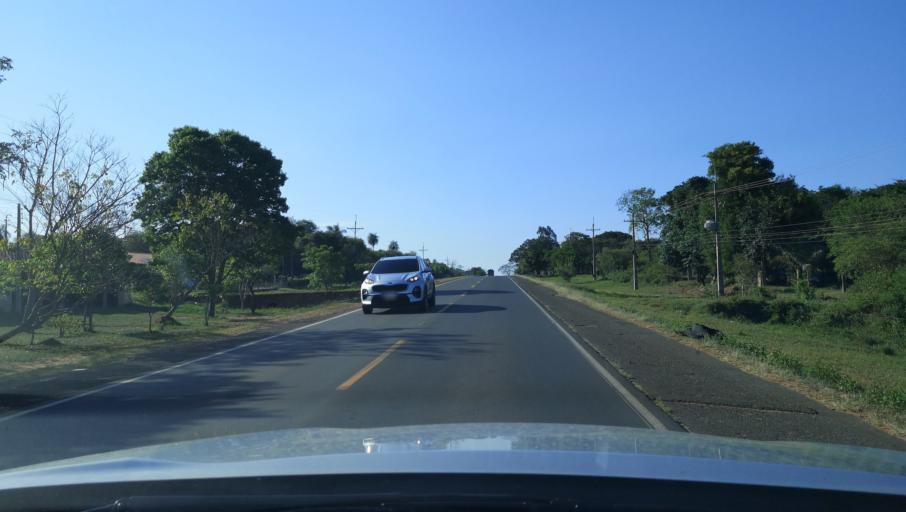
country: PY
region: Misiones
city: Santa Maria
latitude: -26.8656
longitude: -57.0334
